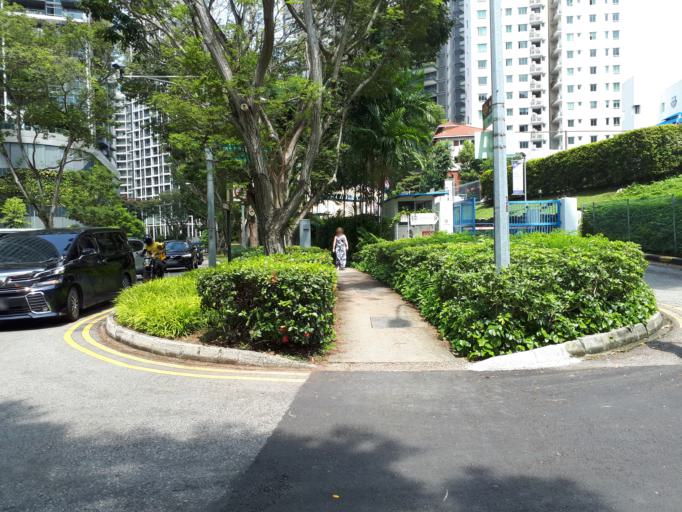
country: SG
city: Singapore
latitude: 1.3025
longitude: 103.8379
